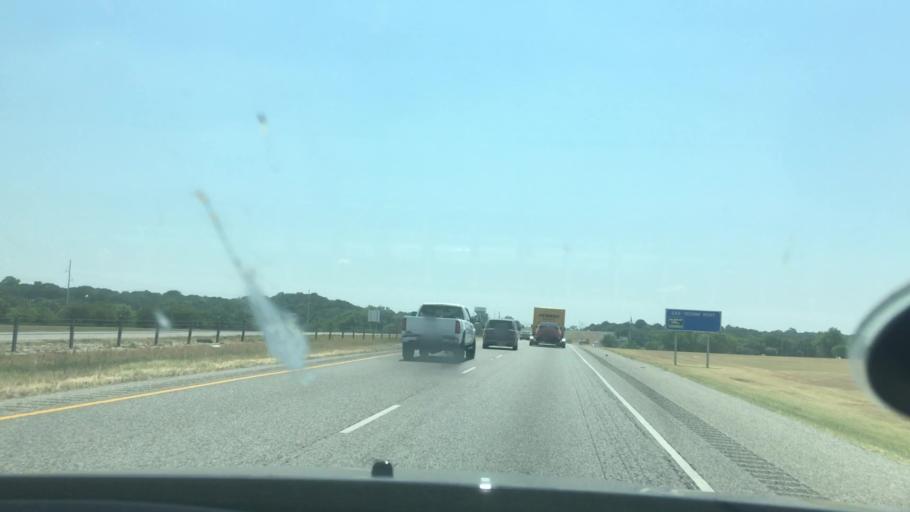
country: US
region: Oklahoma
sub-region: Bryan County
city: Durant
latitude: 34.0221
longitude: -96.3887
